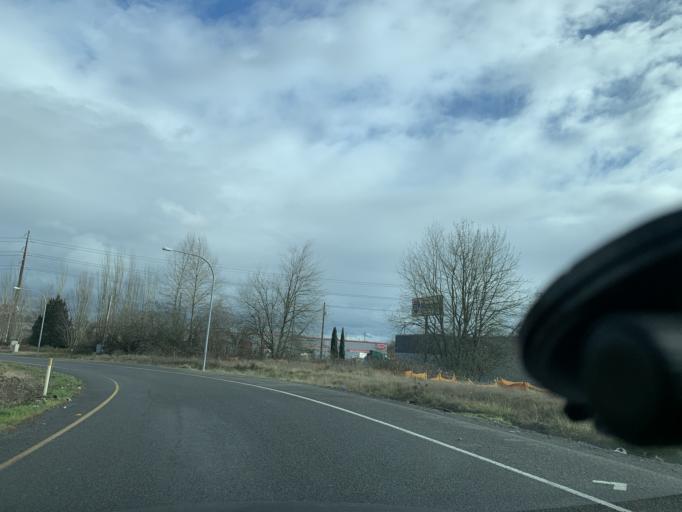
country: US
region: Washington
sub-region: Pierce County
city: Fife
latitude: 47.2397
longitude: -122.3848
